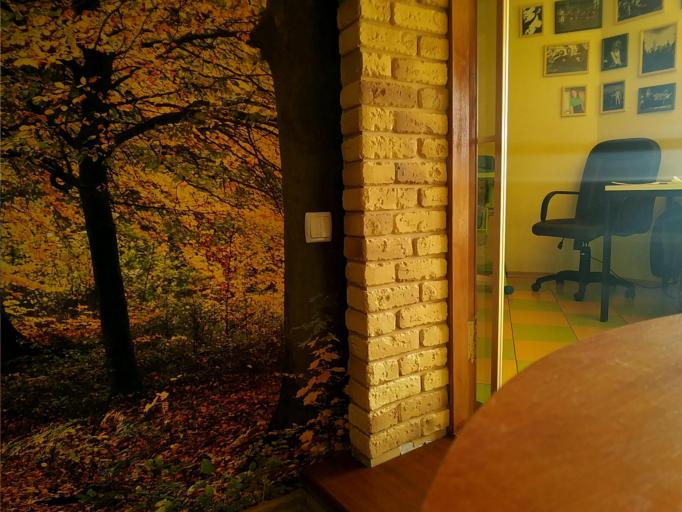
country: RU
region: Smolensk
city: Safonovo
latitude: 55.0980
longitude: 33.0872
